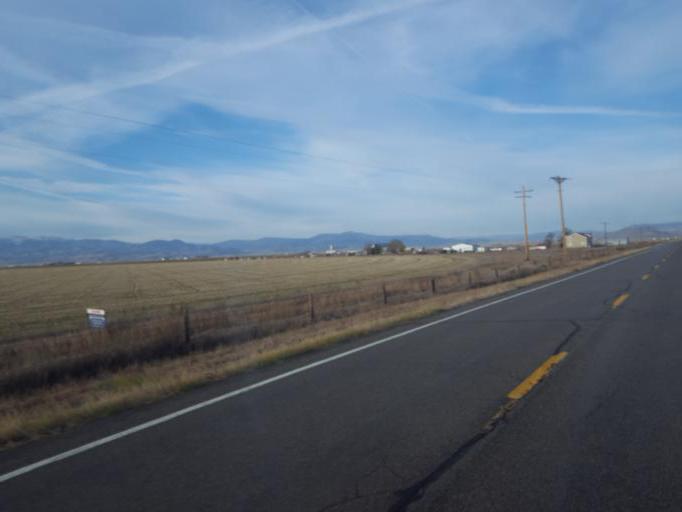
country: US
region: Colorado
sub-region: Saguache County
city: Center
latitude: 37.7482
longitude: -106.1618
